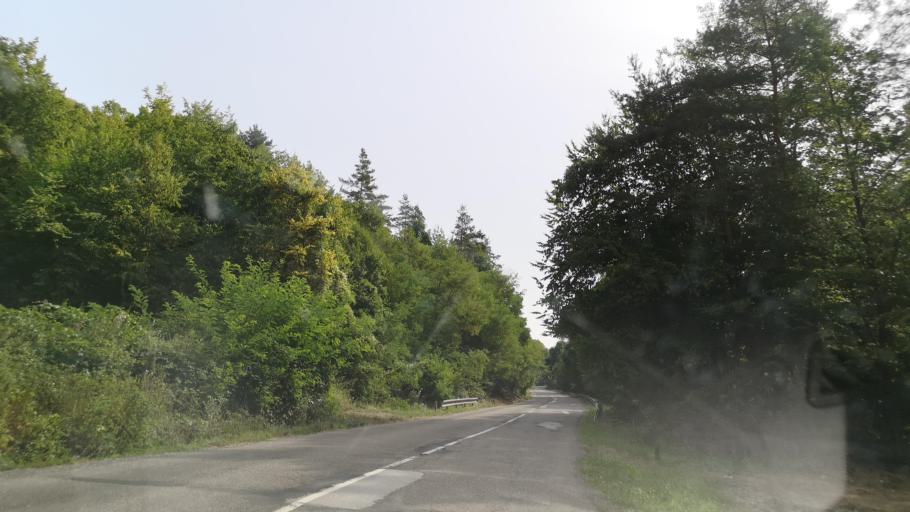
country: SK
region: Banskobystricky
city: Revuca
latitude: 48.5854
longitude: 20.0737
